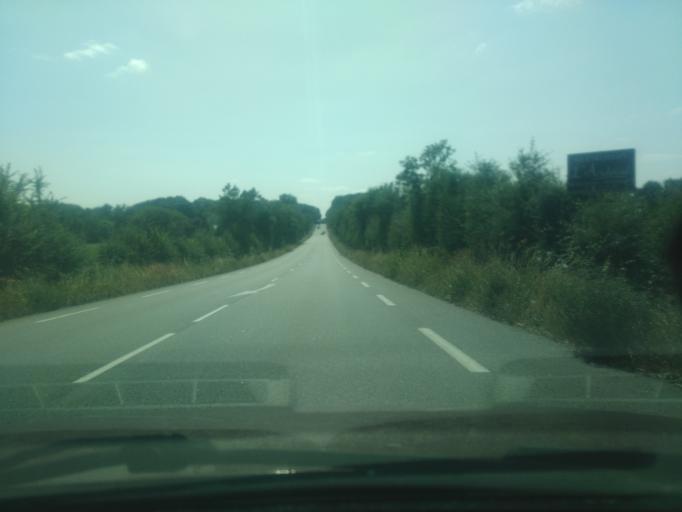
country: FR
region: Pays de la Loire
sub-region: Departement de la Vendee
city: Les Essarts
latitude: 46.7797
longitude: -1.2150
